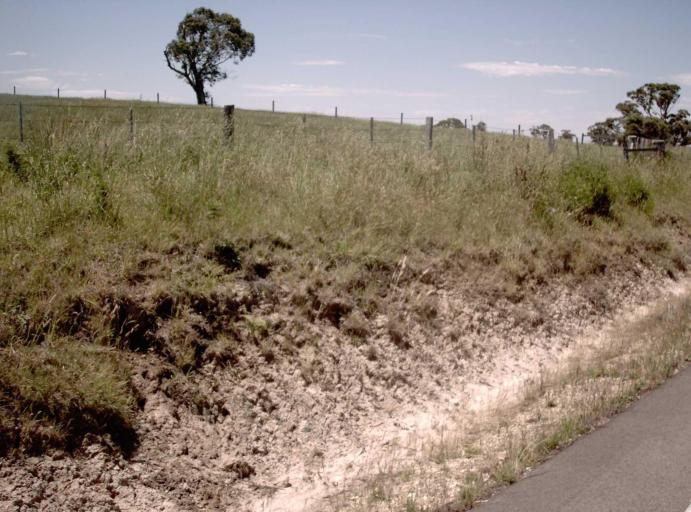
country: AU
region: Victoria
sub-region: East Gippsland
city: Lakes Entrance
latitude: -37.7065
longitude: 148.4995
